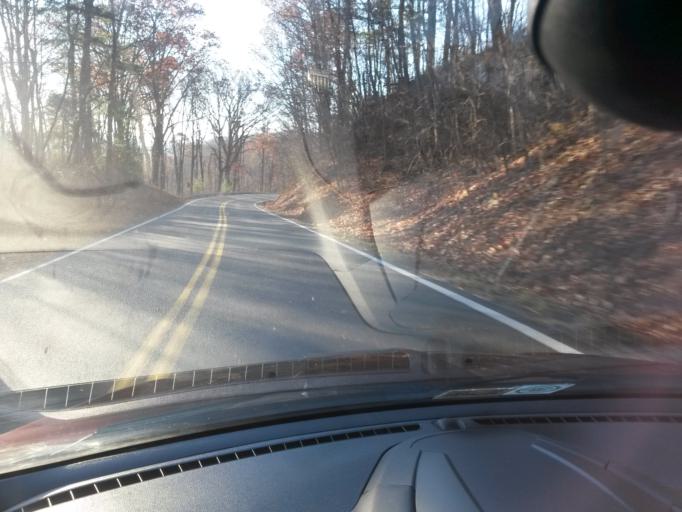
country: US
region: Virginia
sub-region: City of Buena Vista
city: Buena Vista
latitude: 37.7063
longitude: -79.2481
